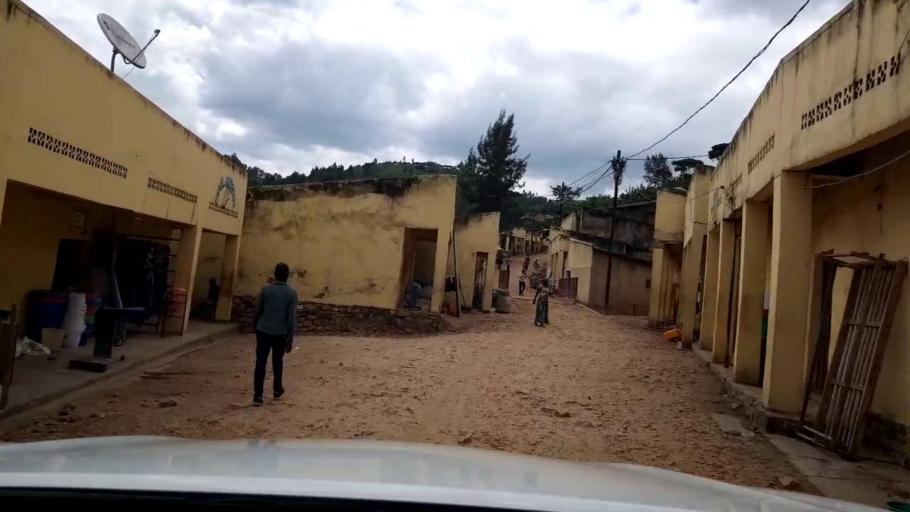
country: RW
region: Southern Province
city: Gitarama
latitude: -1.9425
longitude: 29.6272
